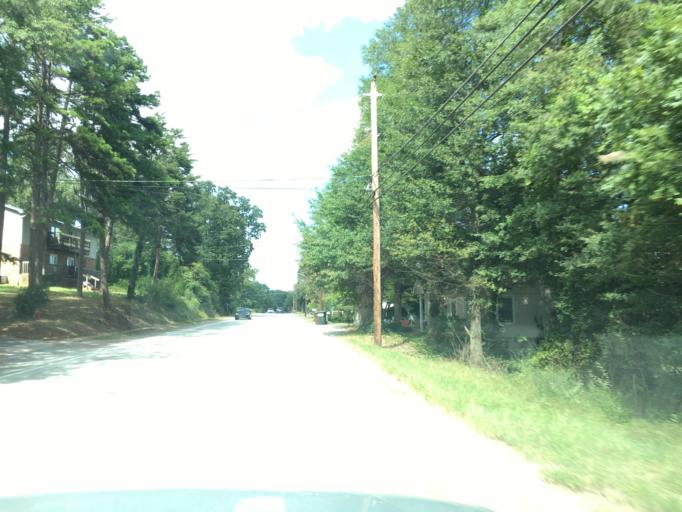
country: US
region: South Carolina
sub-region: Spartanburg County
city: Inman
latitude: 35.0501
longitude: -82.0891
